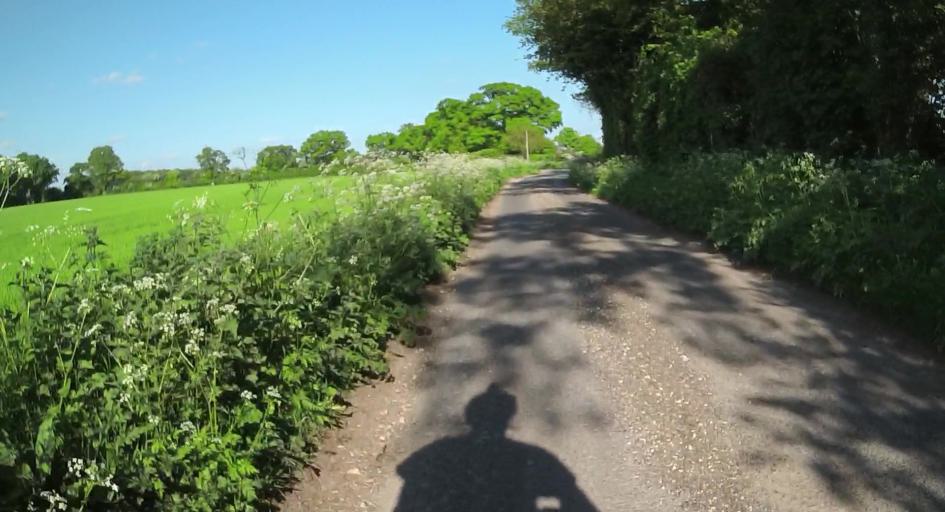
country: GB
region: England
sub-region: Hampshire
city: Overton
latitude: 51.1641
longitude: -1.1840
